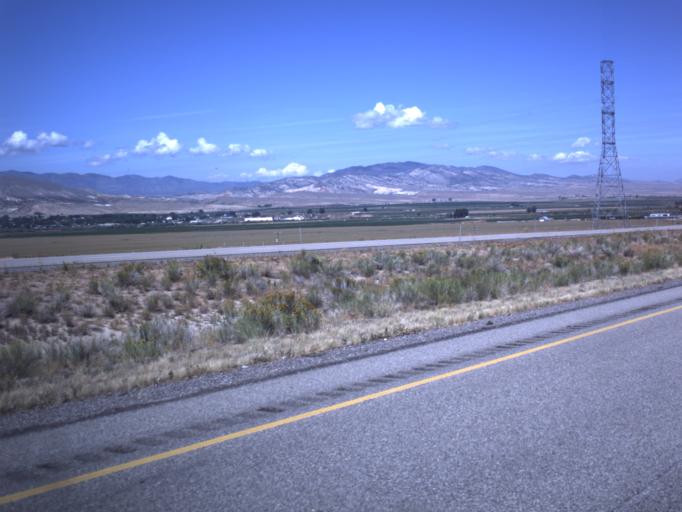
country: US
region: Utah
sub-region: Sevier County
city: Aurora
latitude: 38.8976
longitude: -111.9046
